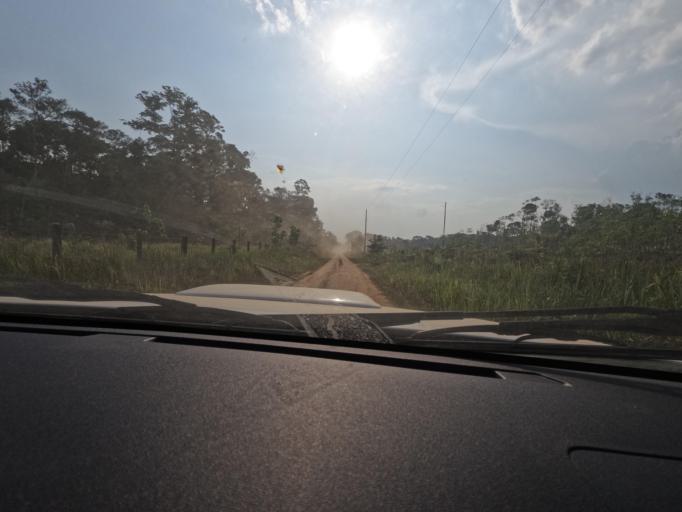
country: BR
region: Rondonia
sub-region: Porto Velho
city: Porto Velho
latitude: -8.5651
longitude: -64.0255
